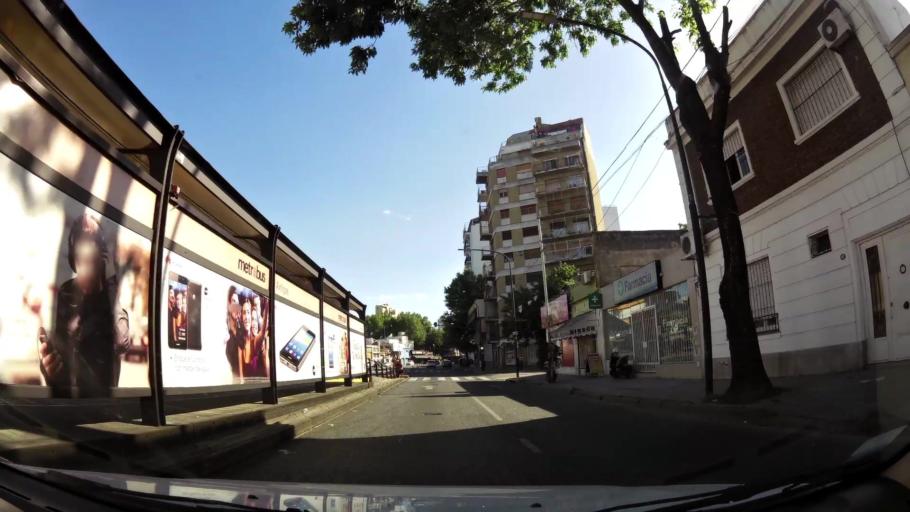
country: AR
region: Buenos Aires F.D.
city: Villa Santa Rita
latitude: -34.6147
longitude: -58.4729
